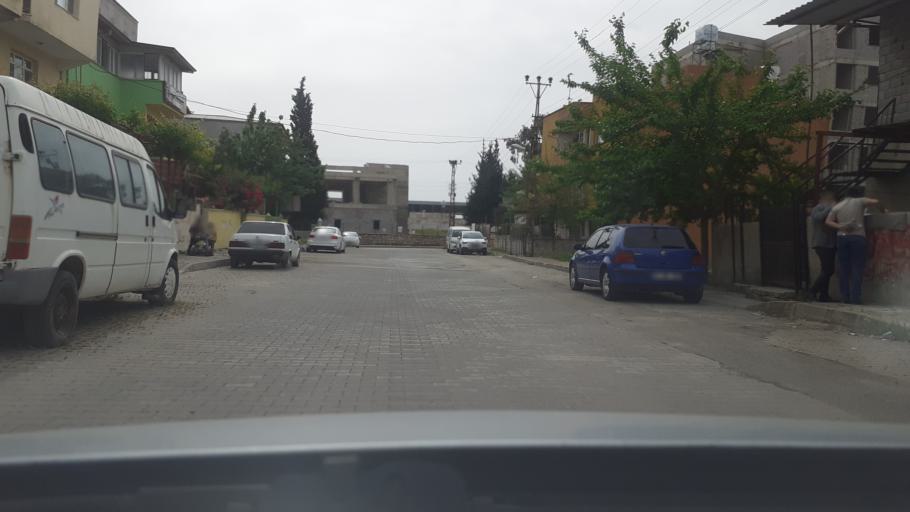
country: TR
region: Hatay
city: Kirikhan
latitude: 36.4939
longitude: 36.3664
